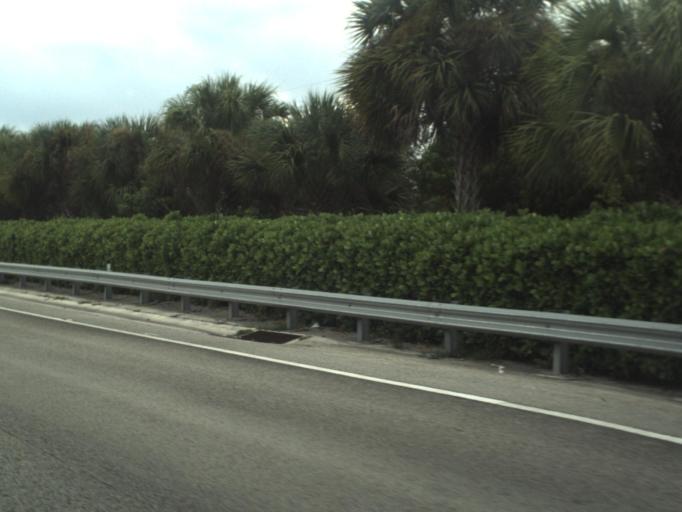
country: US
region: Florida
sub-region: Miami-Dade County
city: Glenvar Heights
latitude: 25.6956
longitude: -80.3147
